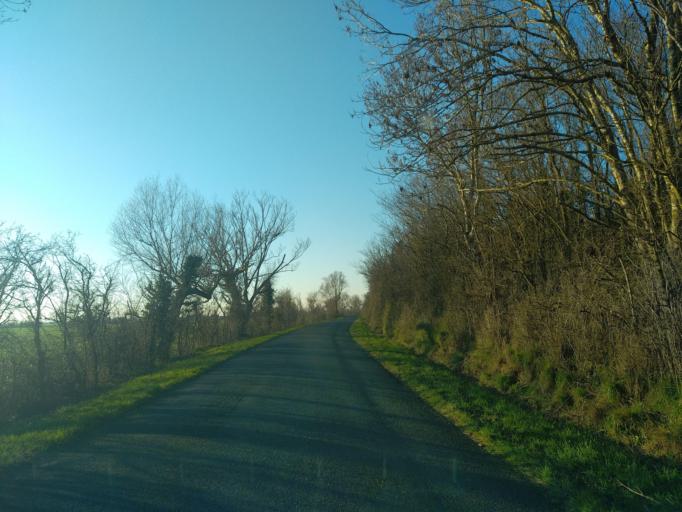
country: FR
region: Pays de la Loire
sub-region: Departement de la Vendee
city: Triaize
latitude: 46.3930
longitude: -1.2913
